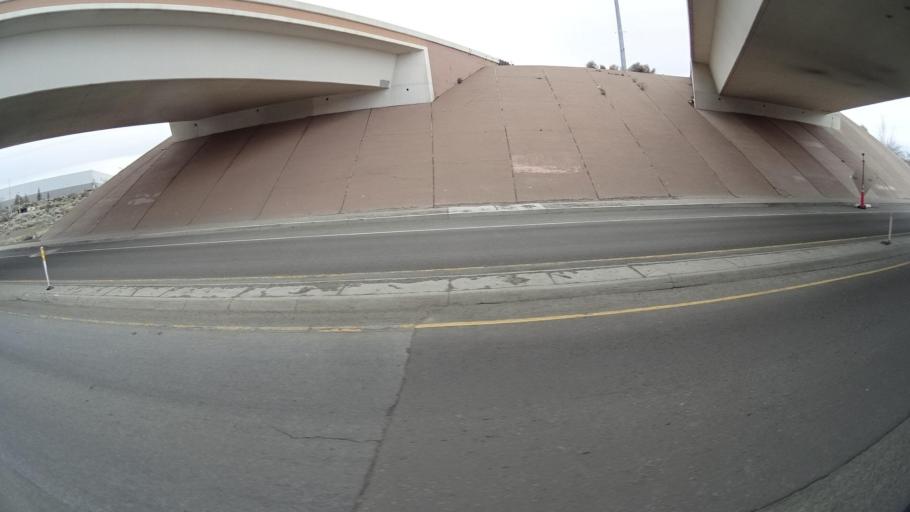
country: US
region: Nevada
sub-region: Washoe County
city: Golden Valley
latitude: 39.6016
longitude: -119.8365
